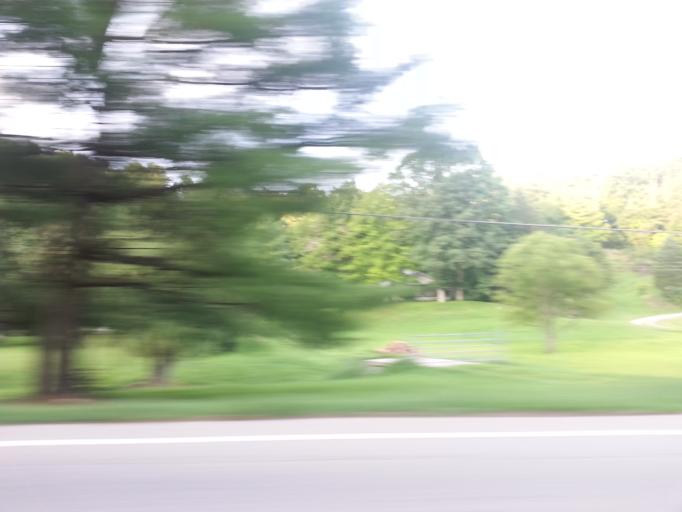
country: US
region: Tennessee
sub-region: Anderson County
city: Norris
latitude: 36.1617
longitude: -84.0331
